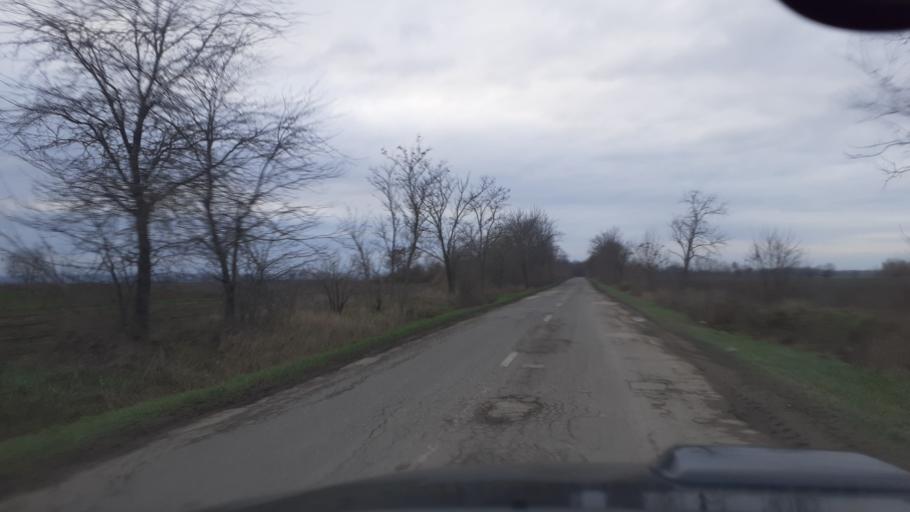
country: HU
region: Bacs-Kiskun
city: Szalkszentmarton
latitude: 46.9565
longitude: 19.0448
